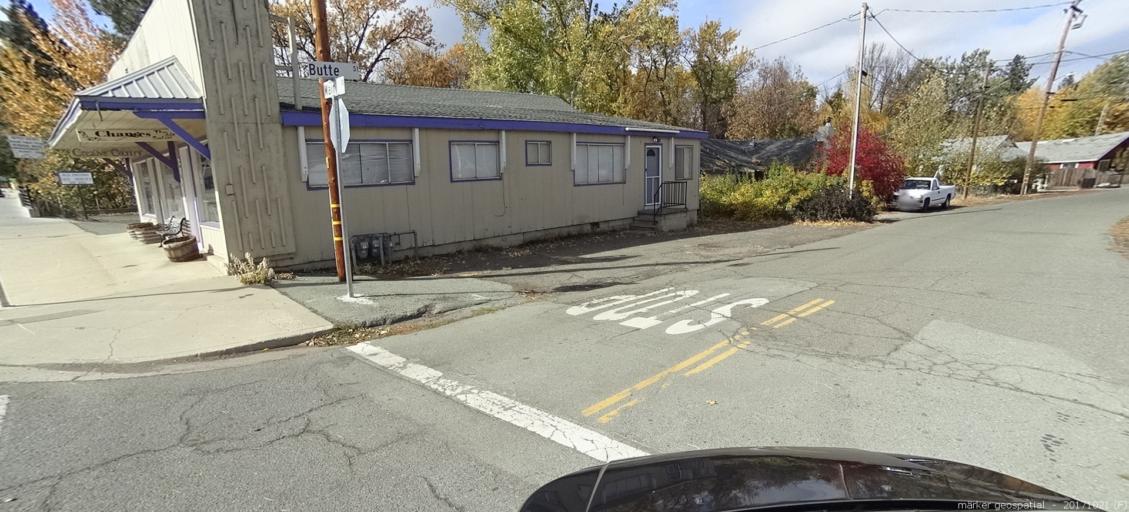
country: US
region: California
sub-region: Shasta County
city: Burney
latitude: 40.8821
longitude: -121.6684
